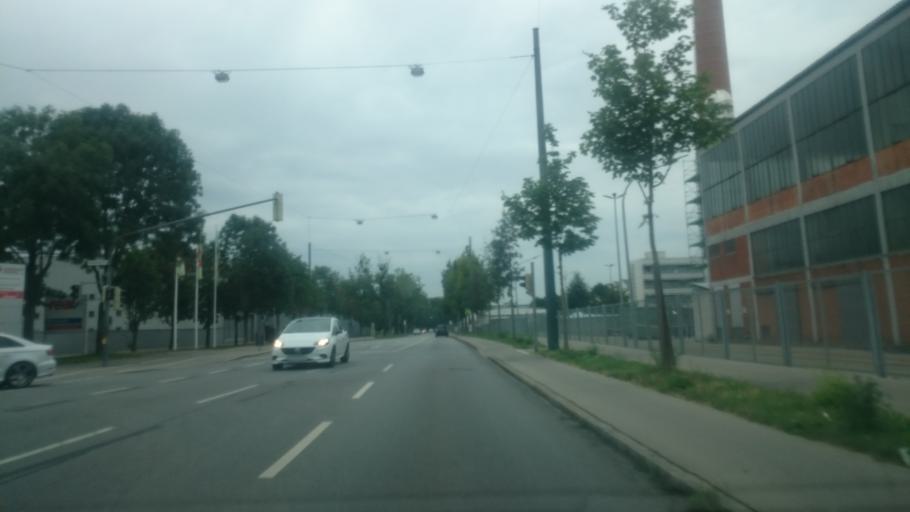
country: DE
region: Bavaria
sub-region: Swabia
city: Augsburg
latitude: 48.3635
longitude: 10.9299
